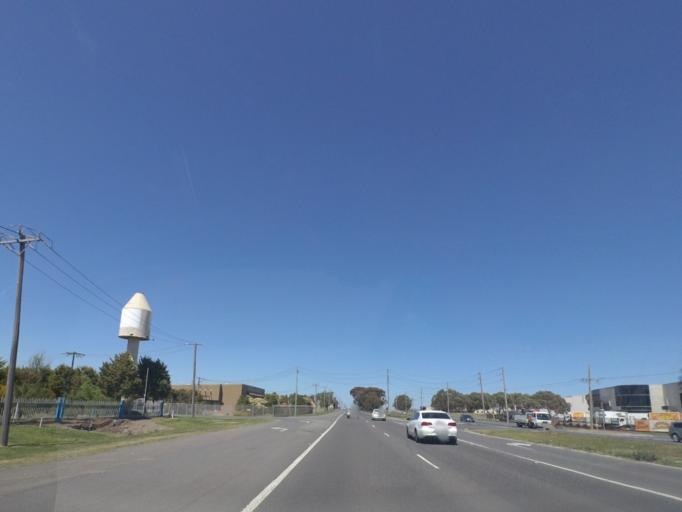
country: AU
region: Victoria
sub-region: Hume
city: Craigieburn
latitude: -37.6214
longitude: 144.9480
